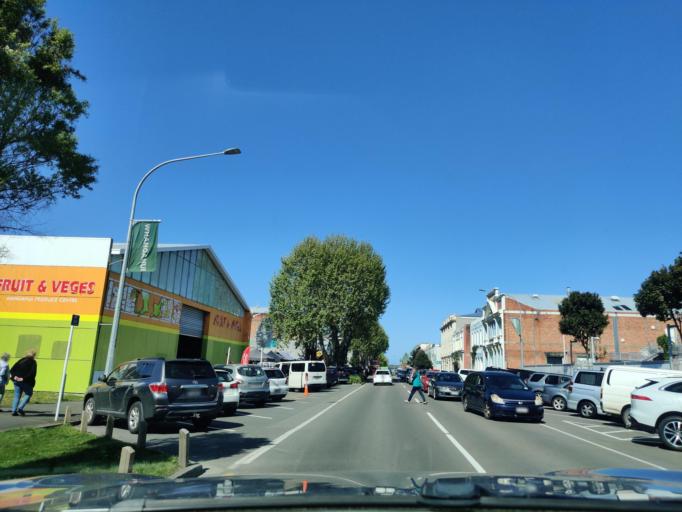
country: NZ
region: Manawatu-Wanganui
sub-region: Wanganui District
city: Wanganui
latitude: -39.9329
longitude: 175.0573
